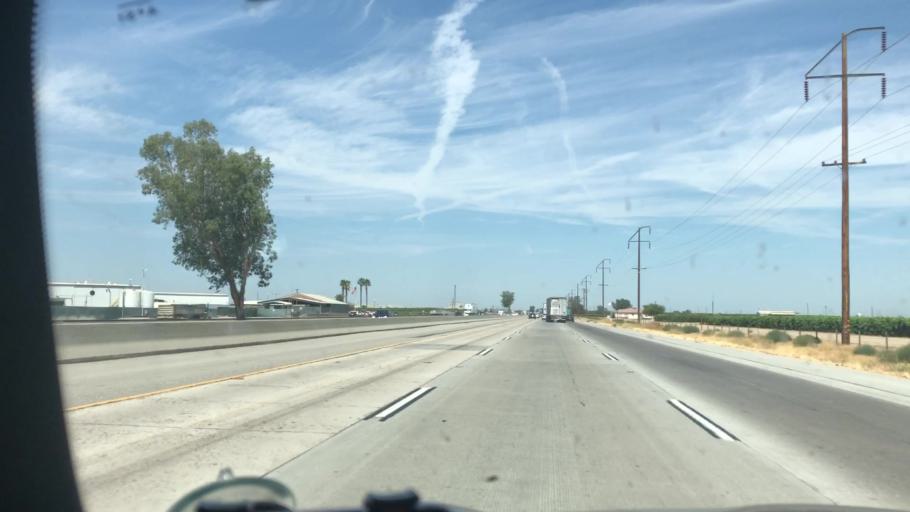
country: US
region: California
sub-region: Kern County
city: Rosedale
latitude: 35.4833
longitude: -119.1425
